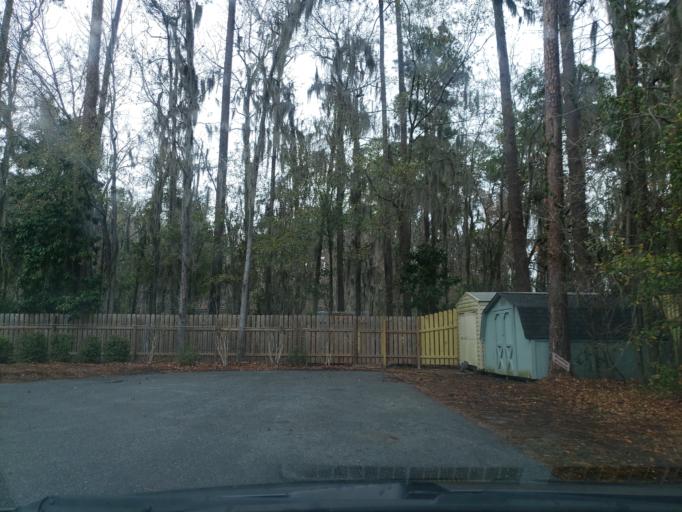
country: US
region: Georgia
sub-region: Chatham County
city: Isle of Hope
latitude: 32.0053
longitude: -81.0914
